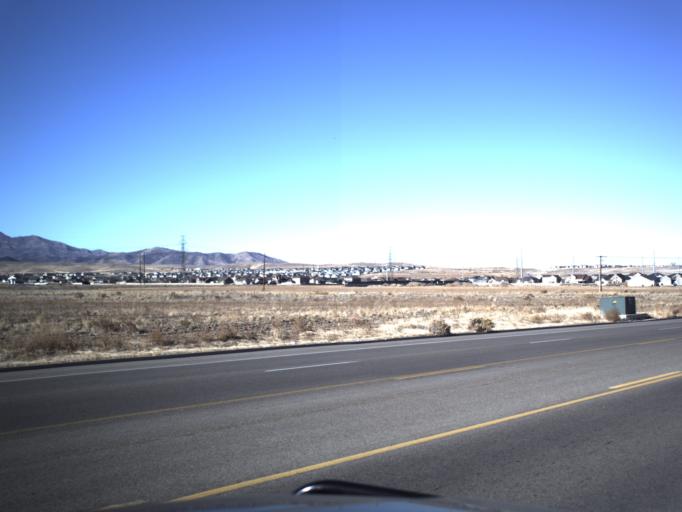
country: US
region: Utah
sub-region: Salt Lake County
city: Oquirrh
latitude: 40.5917
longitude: -112.0241
